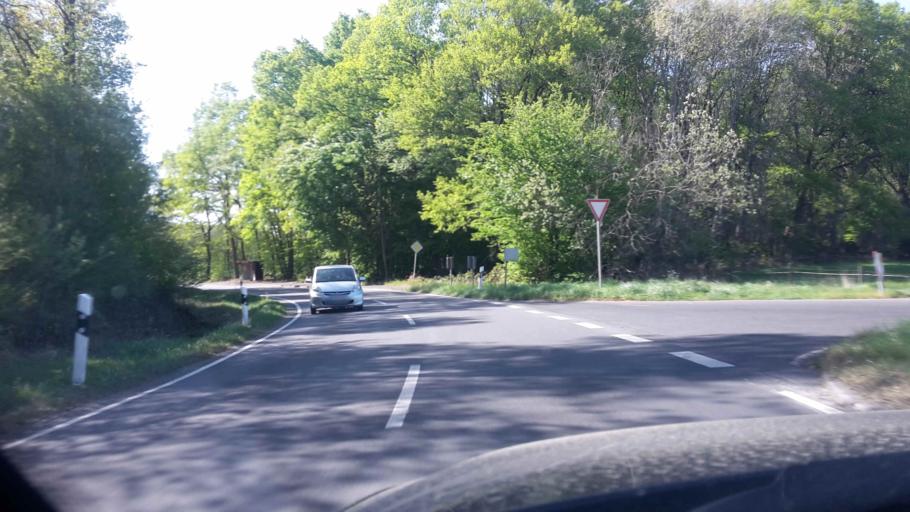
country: DE
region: North Rhine-Westphalia
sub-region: Regierungsbezirk Koln
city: Hennef
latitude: 50.7063
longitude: 7.3171
